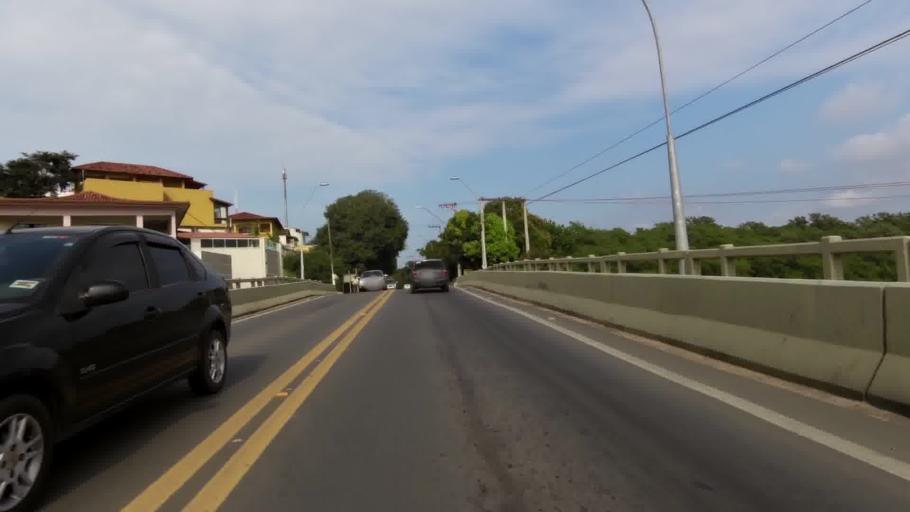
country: BR
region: Espirito Santo
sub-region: Piuma
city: Piuma
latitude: -20.8063
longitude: -40.6558
